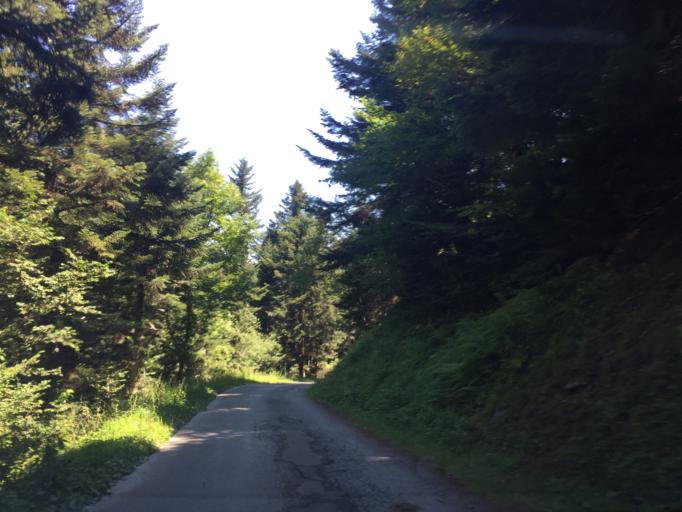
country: FR
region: Midi-Pyrenees
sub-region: Departement des Hautes-Pyrenees
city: Saint-Lary-Soulan
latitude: 42.8487
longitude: 0.2901
